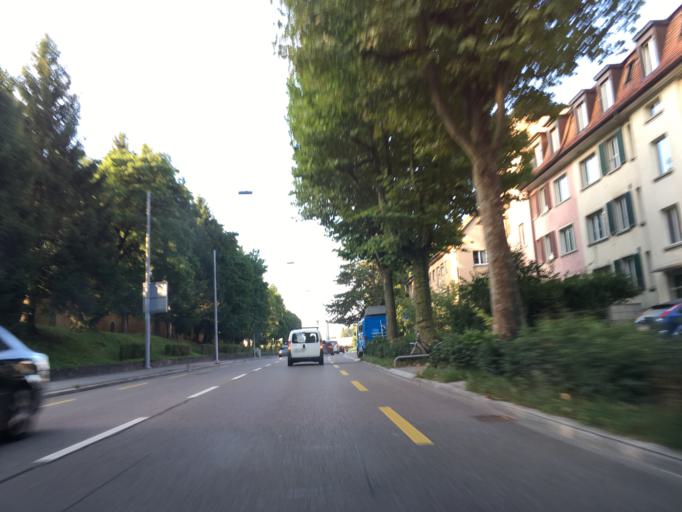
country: CH
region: Zurich
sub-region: Bezirk Zuerich
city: Zuerich (Kreis 2) / Wollishofen
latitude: 47.3333
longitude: 8.5299
